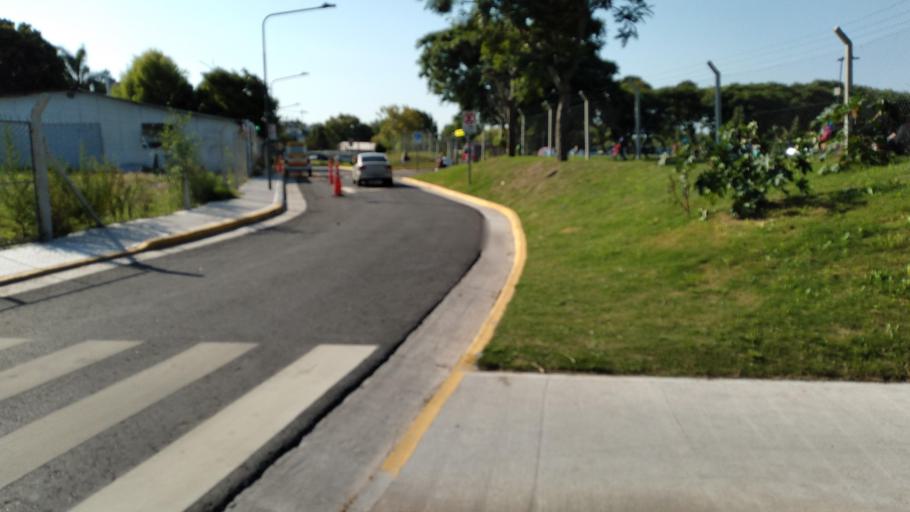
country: AR
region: Buenos Aires
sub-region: Partido de Vicente Lopez
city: Olivos
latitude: -34.5007
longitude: -58.4786
